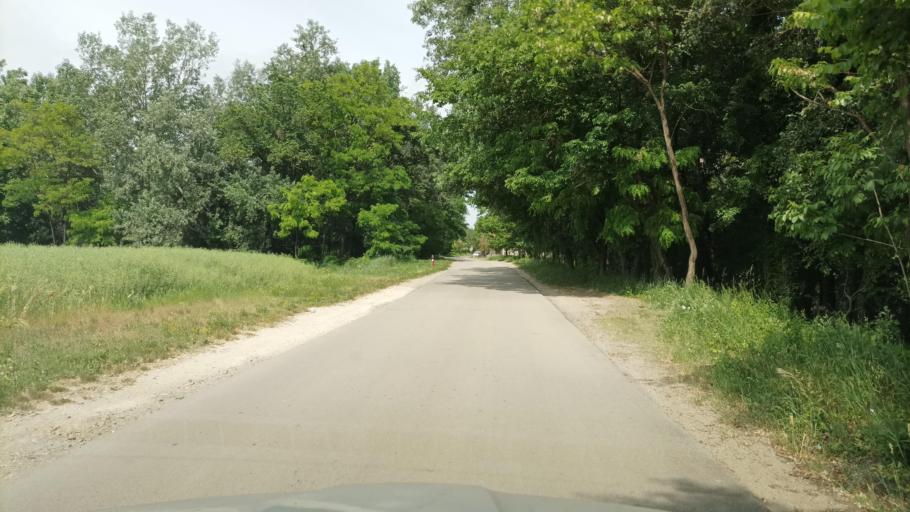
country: HU
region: Pest
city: Rackeve
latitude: 47.1258
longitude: 18.9544
